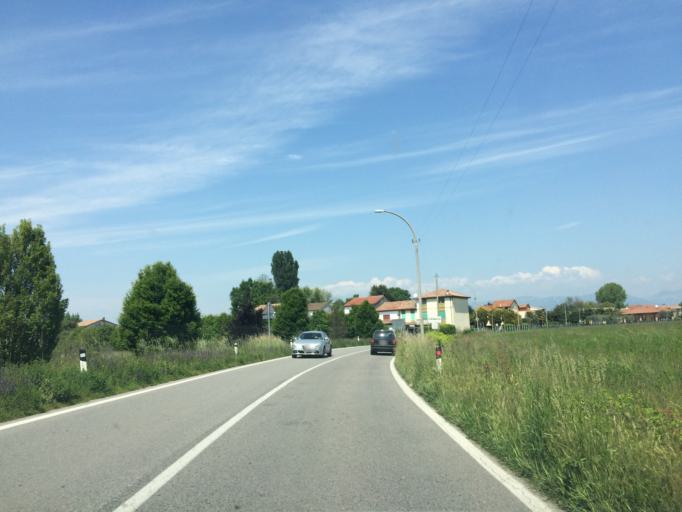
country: IT
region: Veneto
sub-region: Provincia di Padova
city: Fontaniva
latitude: 45.6297
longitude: 11.7621
